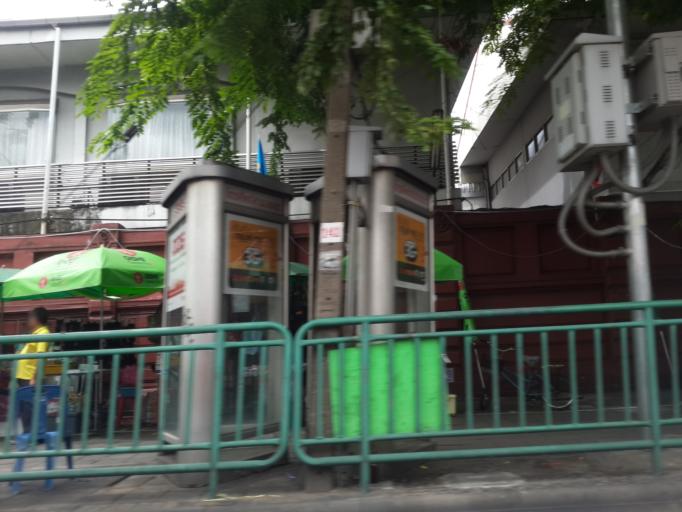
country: TH
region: Bangkok
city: Dusit
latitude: 13.7774
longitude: 100.5107
